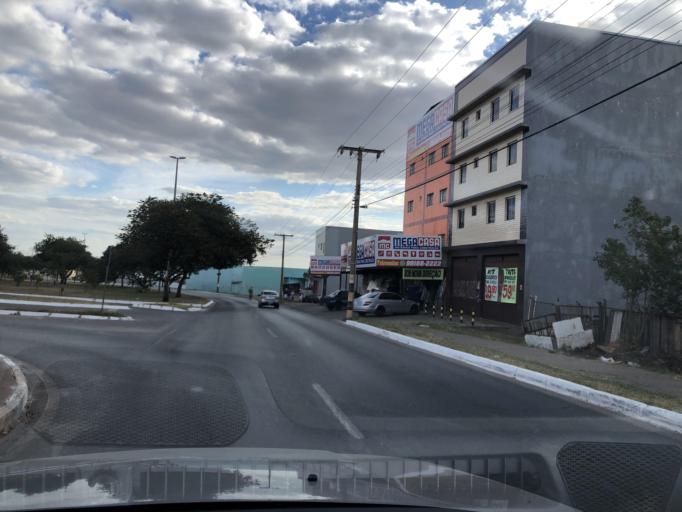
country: BR
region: Federal District
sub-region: Brasilia
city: Brasilia
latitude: -15.8724
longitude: -48.0948
